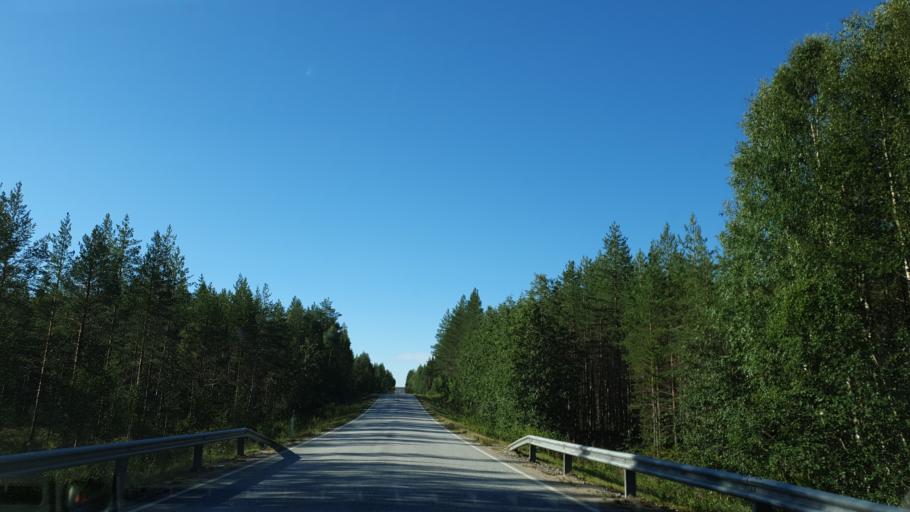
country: FI
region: Kainuu
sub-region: Kehys-Kainuu
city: Kuhmo
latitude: 64.4022
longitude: 29.4678
